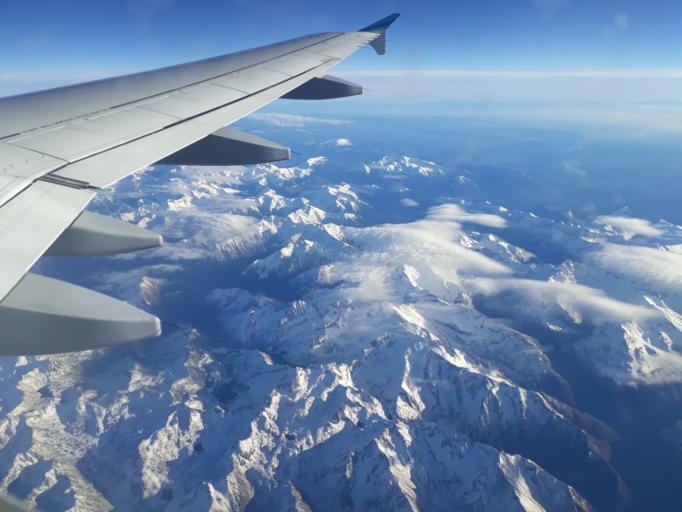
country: FR
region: Midi-Pyrenees
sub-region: Departement des Hautes-Pyrenees
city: Luz-Saint-Sauveur
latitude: 42.9267
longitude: 0.0066
